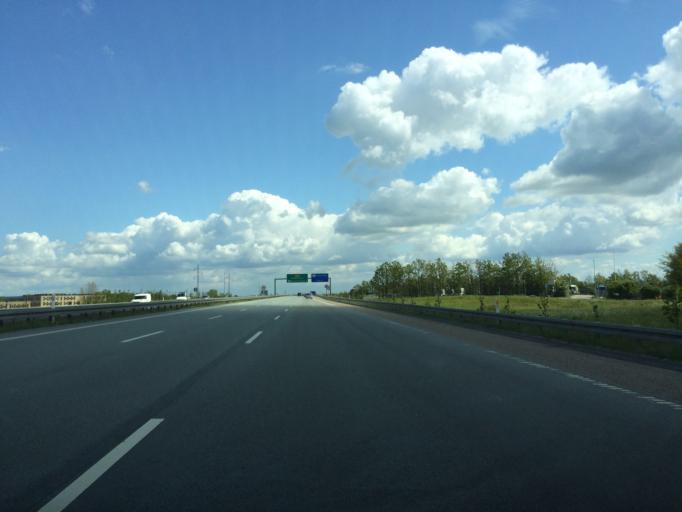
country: DK
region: Zealand
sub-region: Roskilde Kommune
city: Vindinge
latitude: 55.6462
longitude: 12.1372
